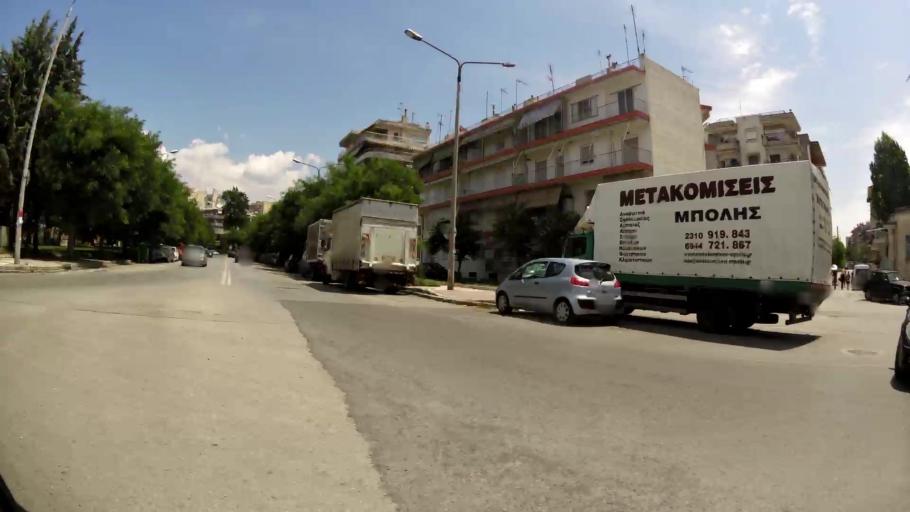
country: GR
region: Central Macedonia
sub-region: Nomos Thessalonikis
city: Triandria
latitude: 40.6179
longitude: 22.9681
